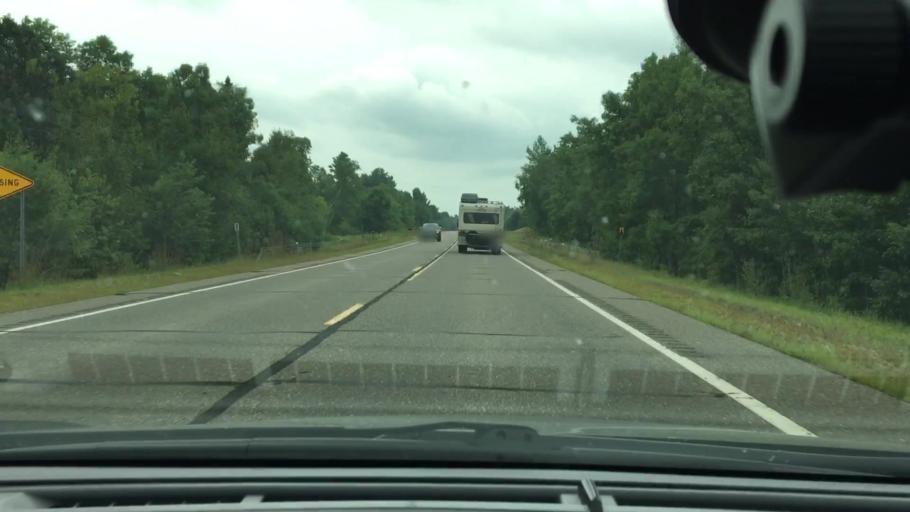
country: US
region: Minnesota
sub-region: Crow Wing County
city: Crosby
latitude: 46.4271
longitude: -93.8734
